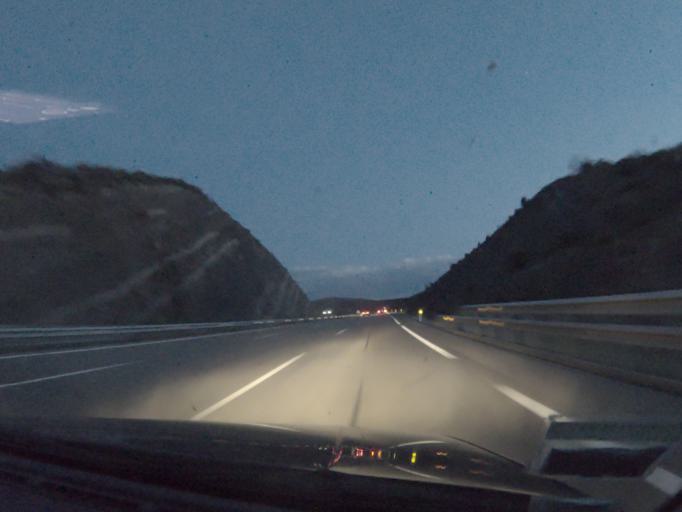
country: ES
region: Castille and Leon
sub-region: Provincia de Leon
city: Folgoso de la Ribera
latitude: 42.6172
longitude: -6.2781
